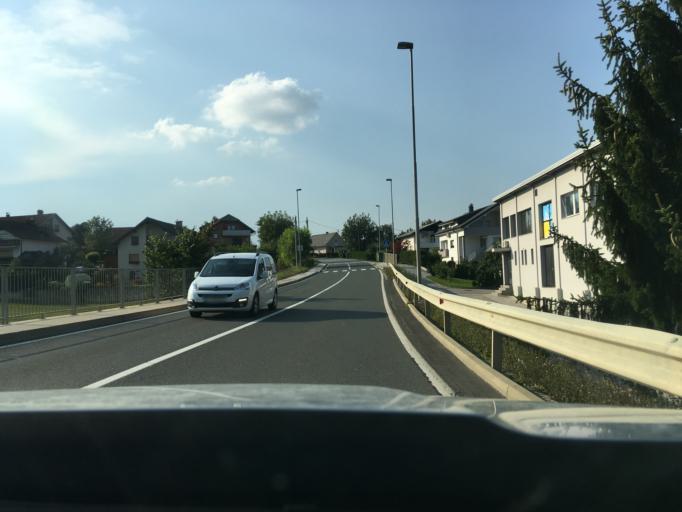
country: SI
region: Novo Mesto
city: Novo Mesto
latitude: 45.7693
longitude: 15.1937
